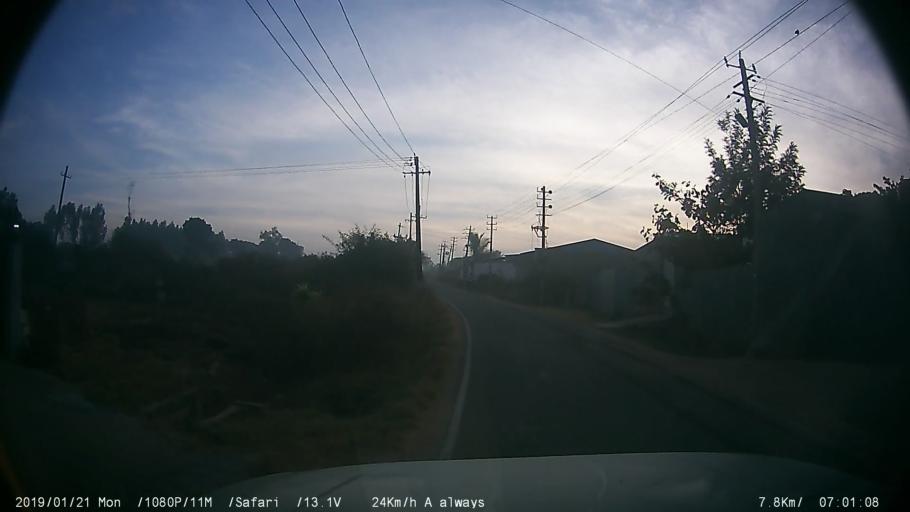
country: IN
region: Karnataka
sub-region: Bangalore Urban
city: Anekal
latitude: 12.8256
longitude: 77.6285
